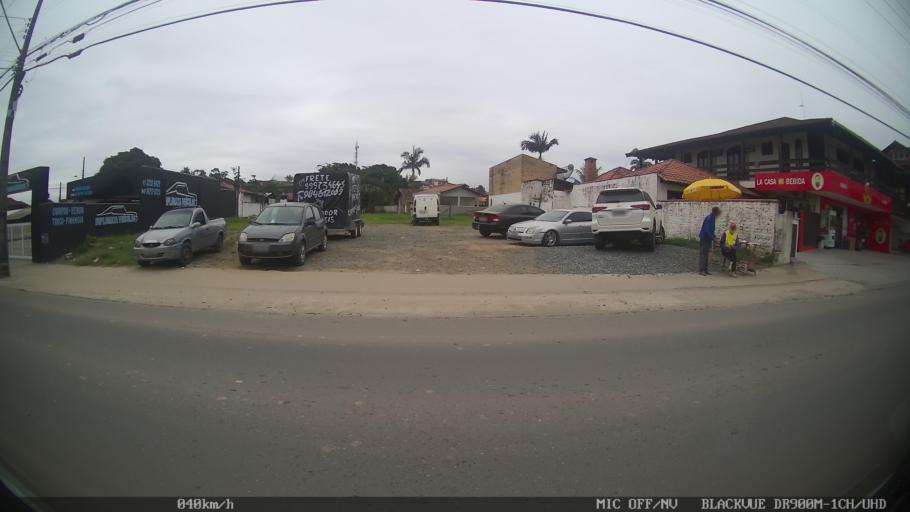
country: BR
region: Santa Catarina
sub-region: Joinville
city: Joinville
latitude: -26.3396
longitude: -48.8099
